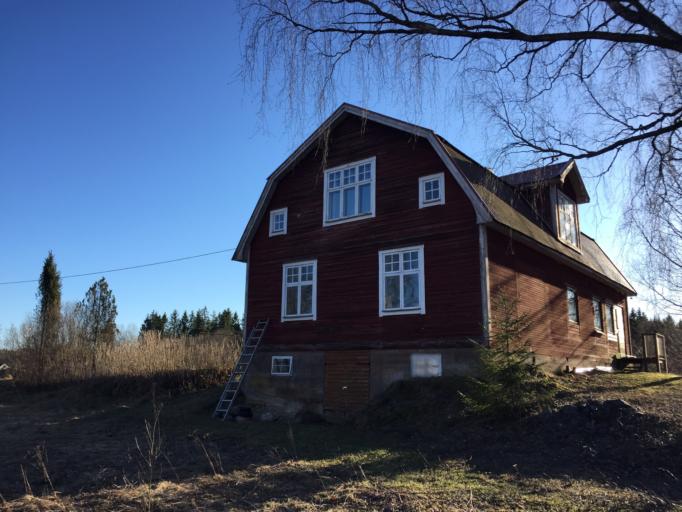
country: SE
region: OEstergoetland
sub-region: Finspangs Kommun
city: Finspang
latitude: 58.8456
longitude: 15.6920
